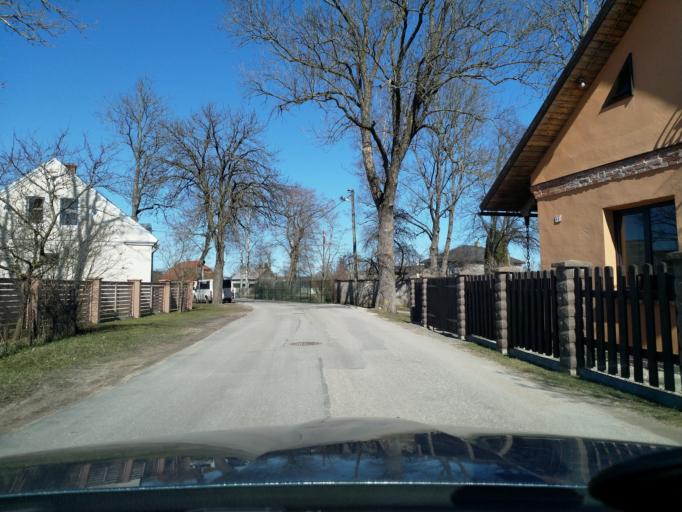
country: LV
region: Kuldigas Rajons
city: Kuldiga
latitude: 56.9647
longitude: 21.9988
